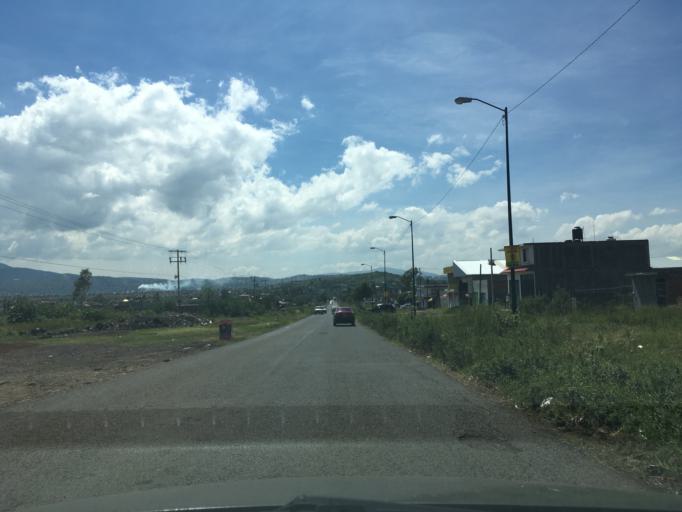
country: MX
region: Michoacan
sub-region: Morelia
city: Villas de la Loma
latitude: 19.6854
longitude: -101.2793
